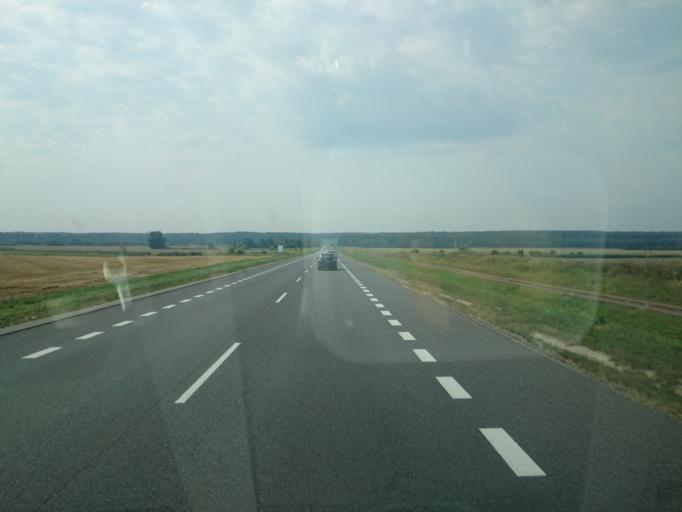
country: PL
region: Lubusz
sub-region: Powiat miedzyrzecki
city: Miedzyrzecz
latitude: 52.4340
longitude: 15.5560
